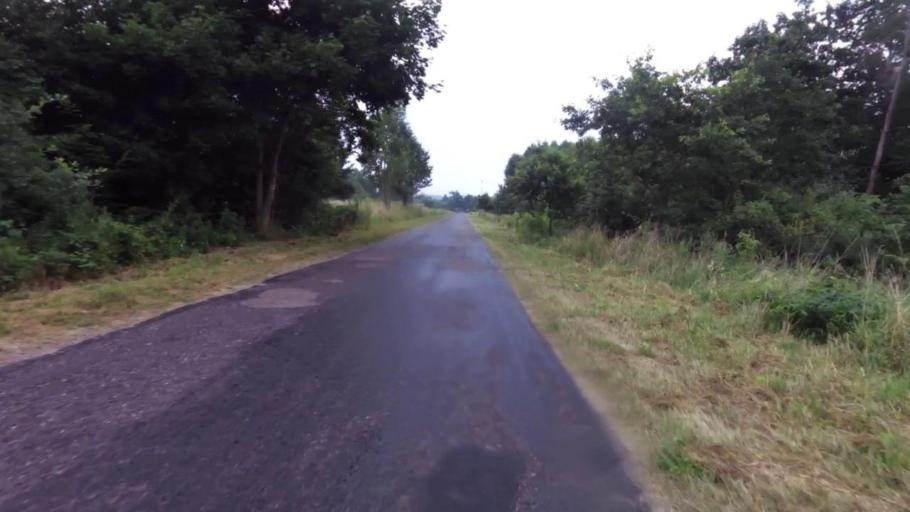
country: PL
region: West Pomeranian Voivodeship
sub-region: Powiat lobeski
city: Wegorzyno
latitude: 53.5344
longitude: 15.6620
